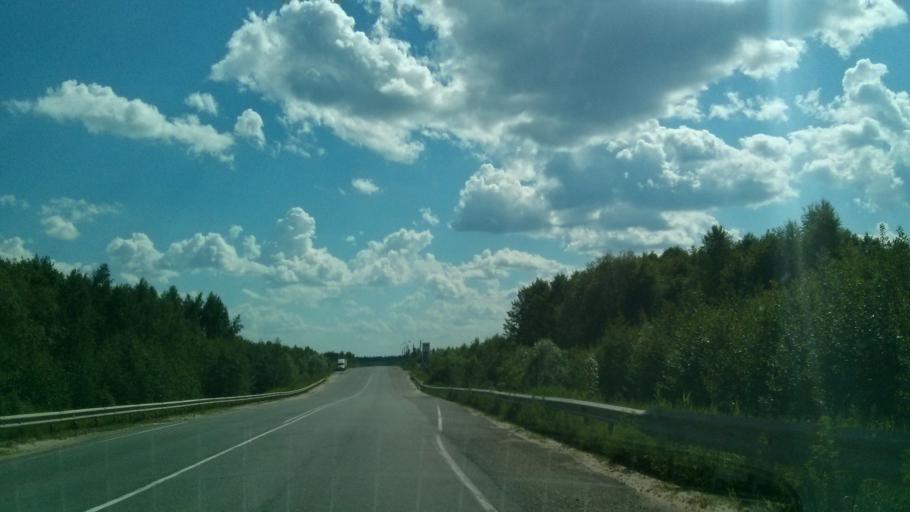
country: RU
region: Vladimir
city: Melenki
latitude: 55.3409
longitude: 41.6680
